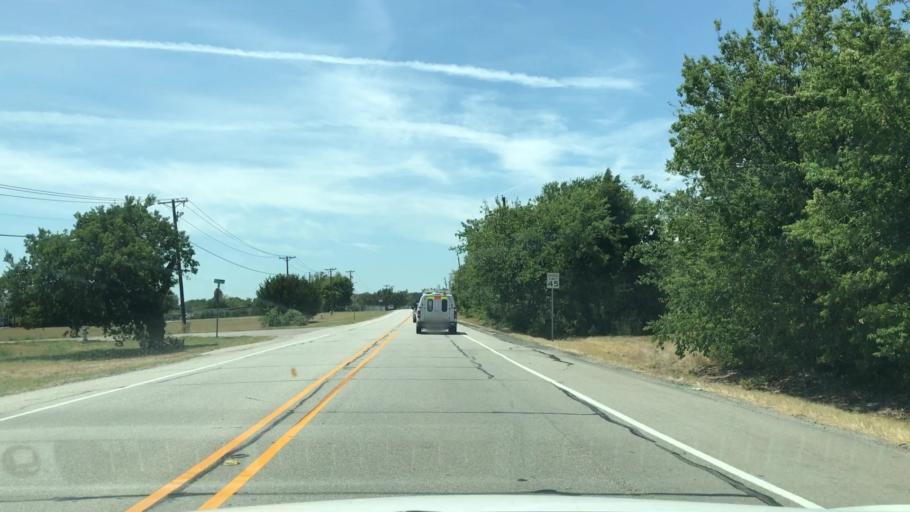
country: US
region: Texas
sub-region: Collin County
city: Fairview
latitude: 33.1636
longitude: -96.6302
